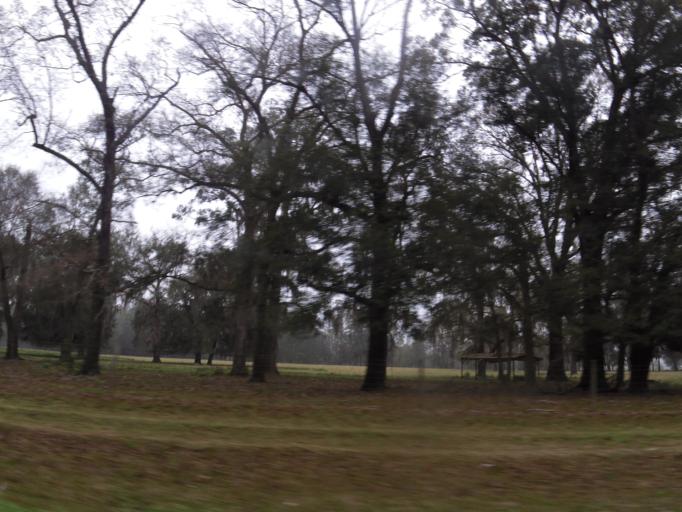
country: US
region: Florida
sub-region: Alachua County
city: Alachua
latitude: 29.8970
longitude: -82.4445
